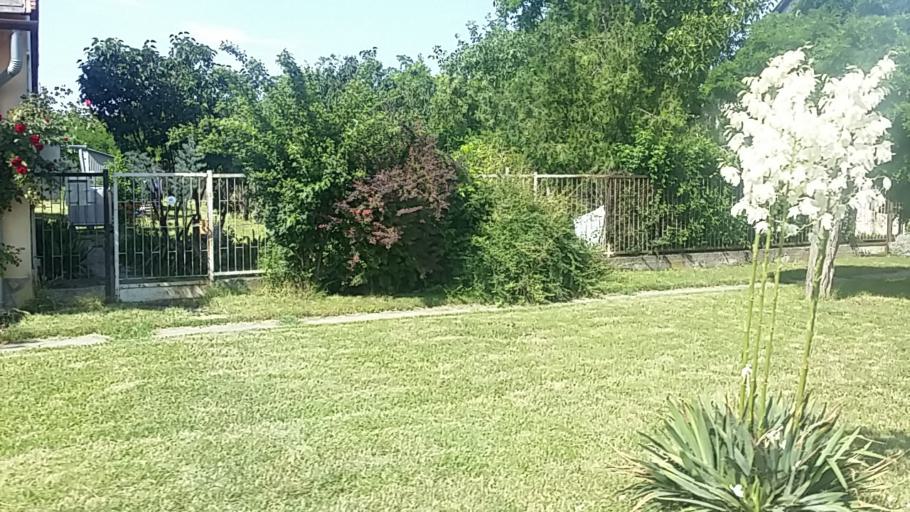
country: HU
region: Fejer
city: Ivancsa
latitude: 47.1834
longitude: 18.8272
